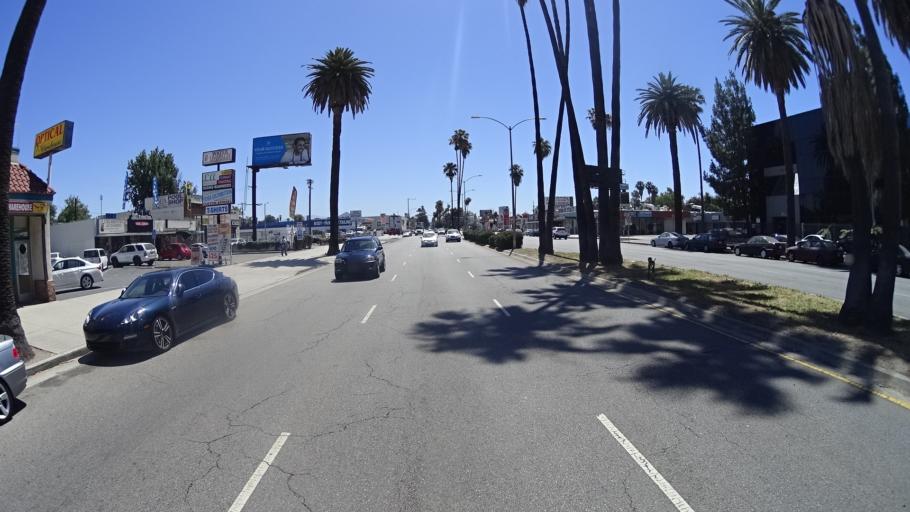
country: US
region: California
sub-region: Los Angeles County
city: Northridge
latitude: 34.2013
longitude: -118.5206
